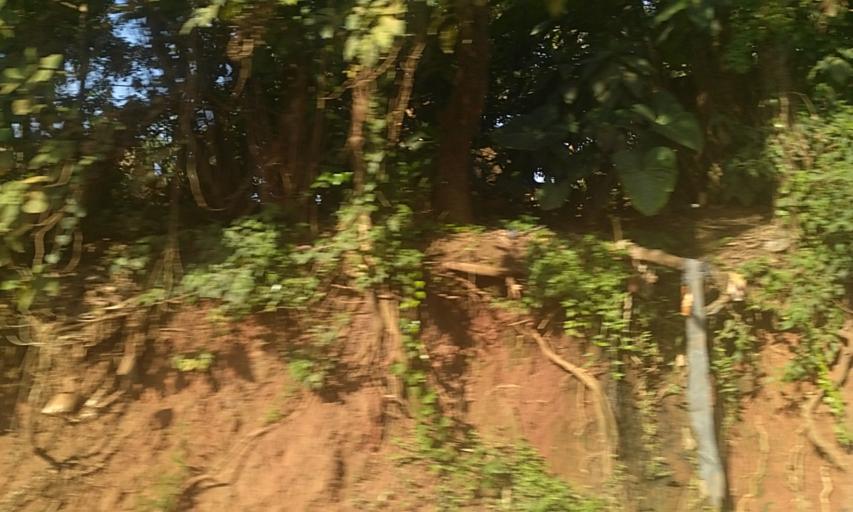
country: UG
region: Central Region
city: Kampala Central Division
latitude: 0.3239
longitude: 32.5410
